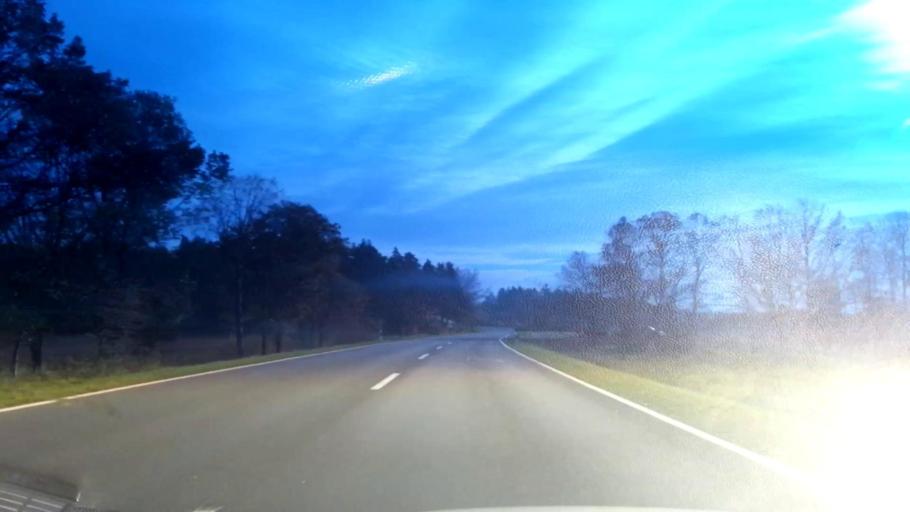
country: DE
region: Bavaria
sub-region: Upper Palatinate
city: Immenreuth
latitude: 49.9118
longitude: 11.8485
